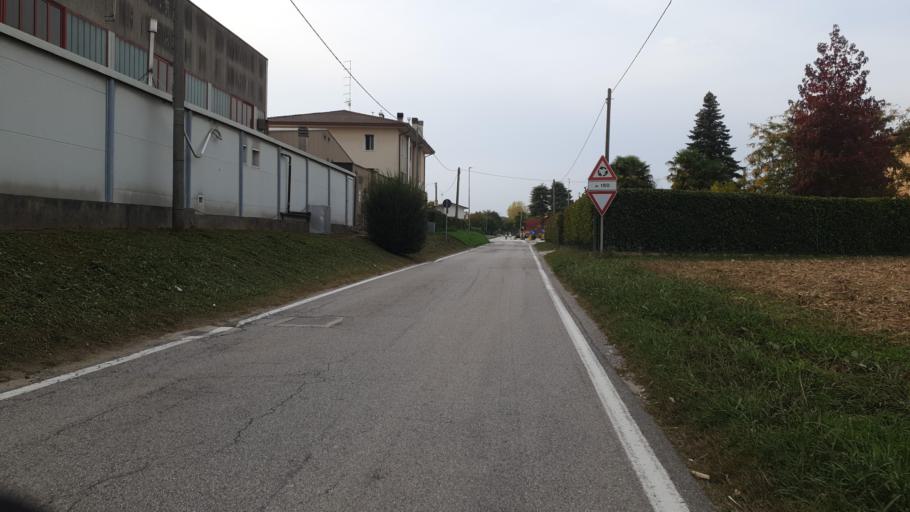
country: IT
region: Veneto
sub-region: Provincia di Padova
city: Villatora
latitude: 45.3907
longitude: 11.9743
